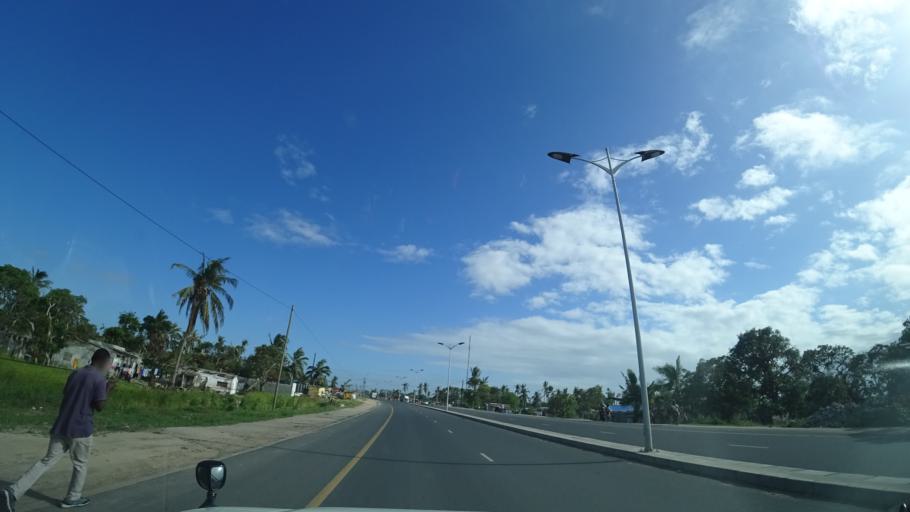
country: MZ
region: Sofala
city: Beira
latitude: -19.7504
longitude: 34.8747
